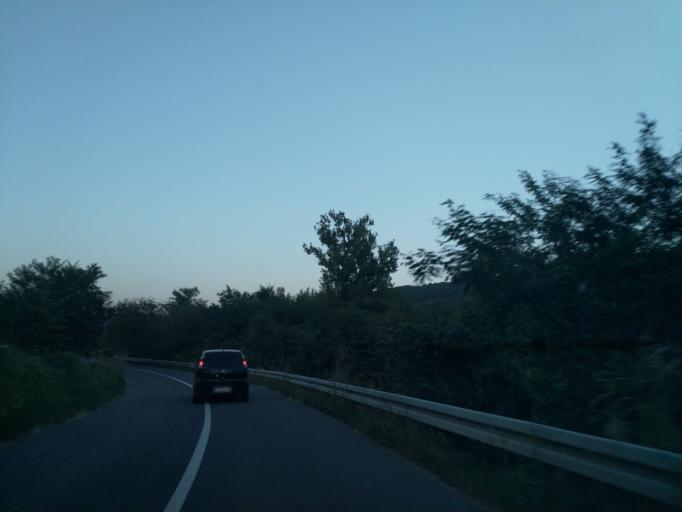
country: RS
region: Central Serbia
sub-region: Rasinski Okrug
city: Krusevac
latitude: 43.6292
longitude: 21.3714
